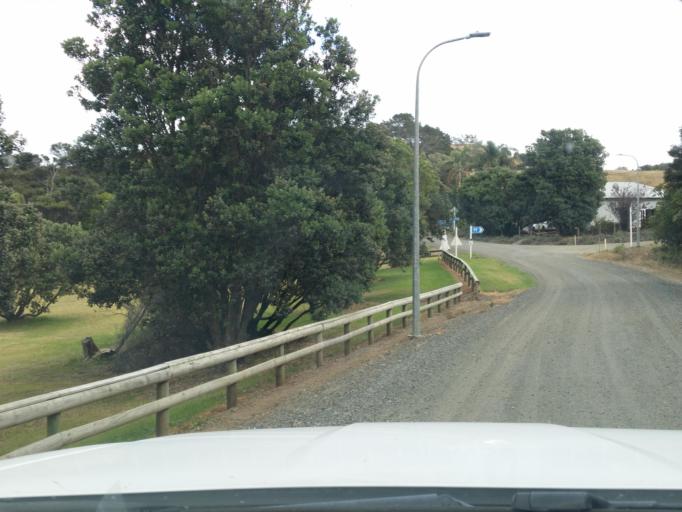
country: NZ
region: Auckland
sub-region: Auckland
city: Wellsford
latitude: -36.3637
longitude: 174.1808
